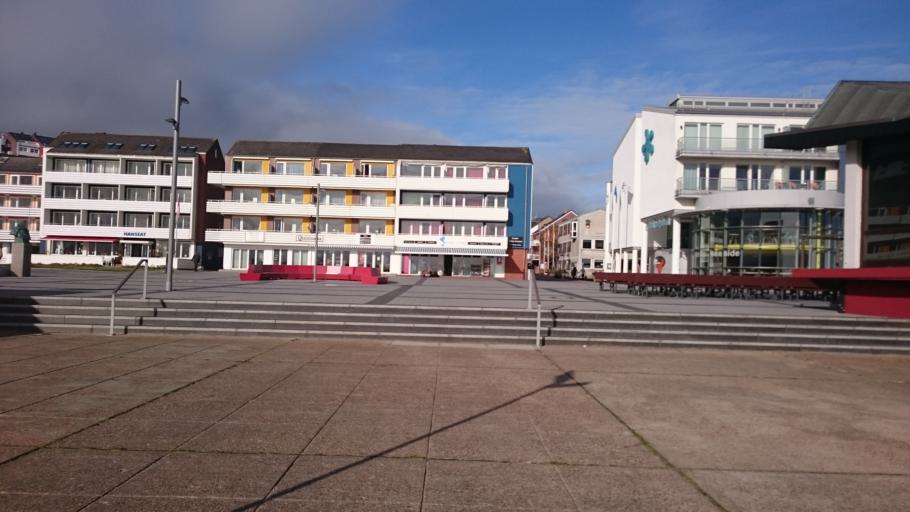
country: DE
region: Schleswig-Holstein
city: Helgoland
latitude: 54.1809
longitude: 7.8910
